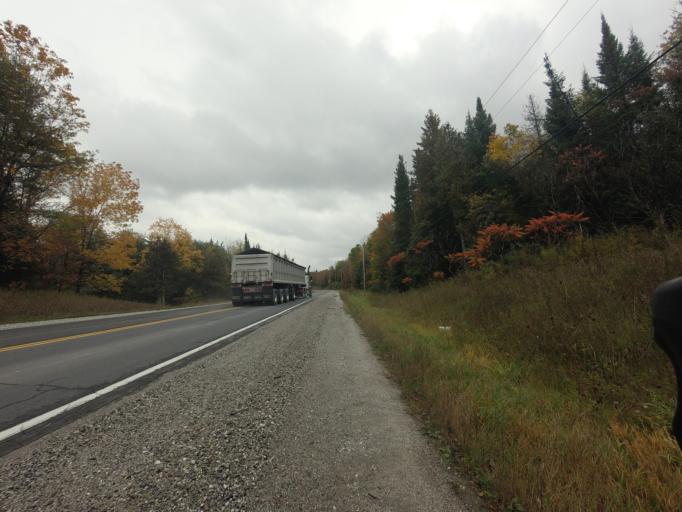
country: CA
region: Ontario
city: Perth
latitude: 45.1177
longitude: -76.4921
